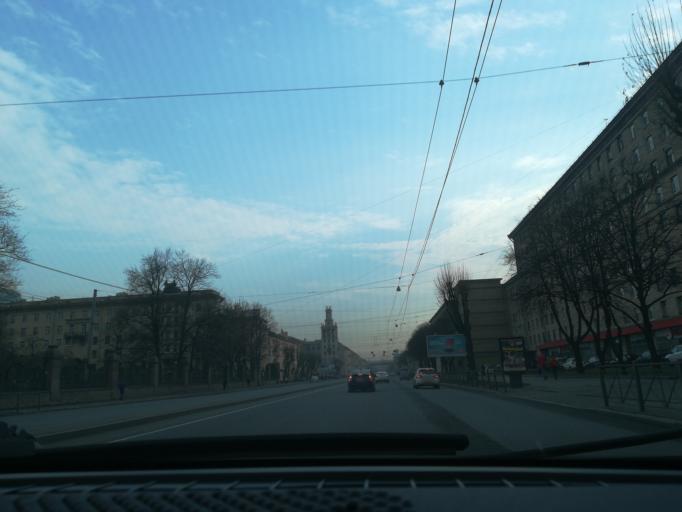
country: RU
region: St.-Petersburg
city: Admiralteisky
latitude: 59.8925
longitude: 30.2736
